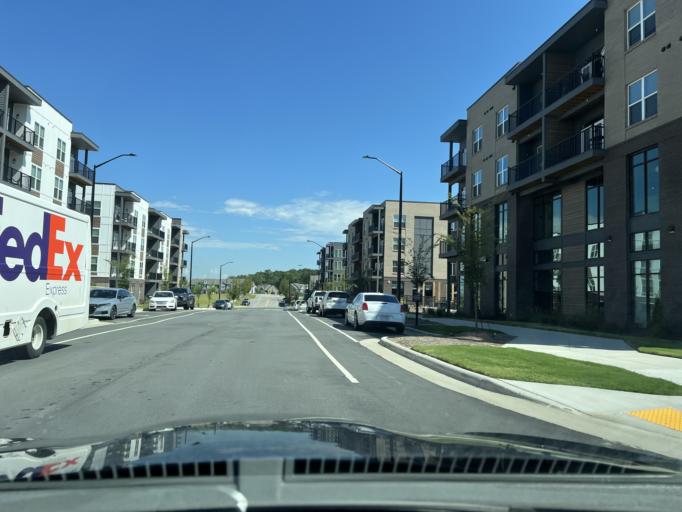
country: US
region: North Carolina
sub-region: Wake County
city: Morrisville
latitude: 35.8782
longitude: -78.8564
